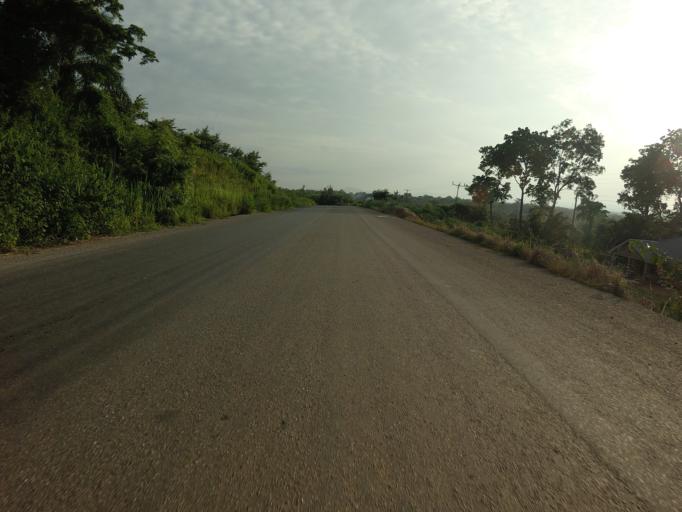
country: GH
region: Volta
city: Kpandu
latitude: 6.9110
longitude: 0.4474
